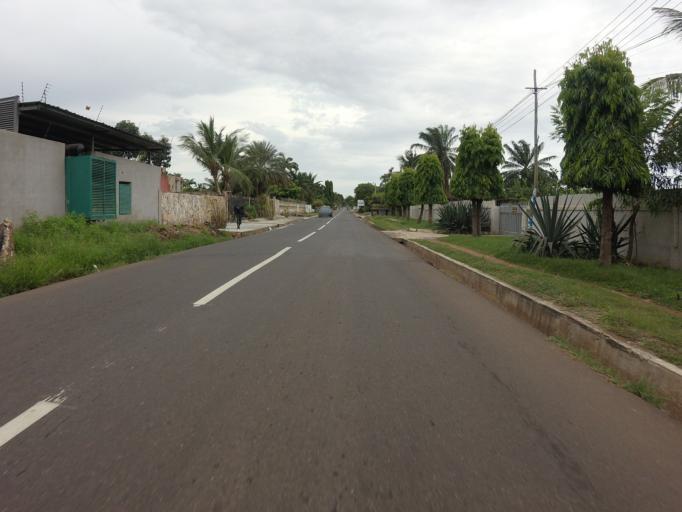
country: GH
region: Greater Accra
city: Dome
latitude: 5.6122
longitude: -0.2084
